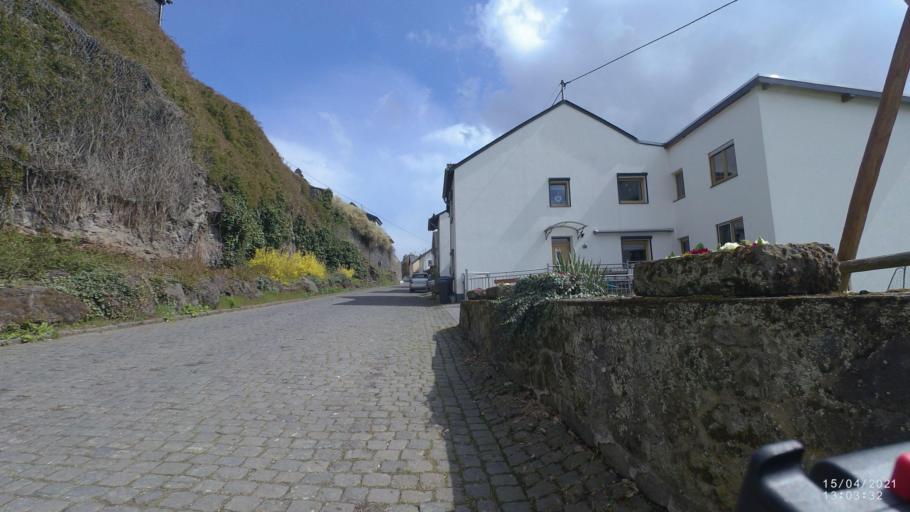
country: DE
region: Rheinland-Pfalz
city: Kottenheim
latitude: 50.3712
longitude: 7.2524
